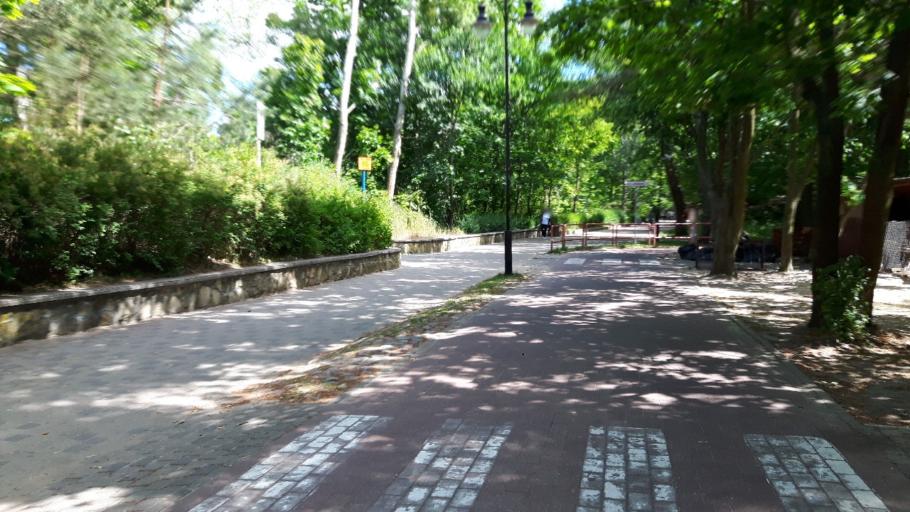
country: PL
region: Pomeranian Voivodeship
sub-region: Sopot
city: Sopot
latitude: 54.4275
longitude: 18.5944
